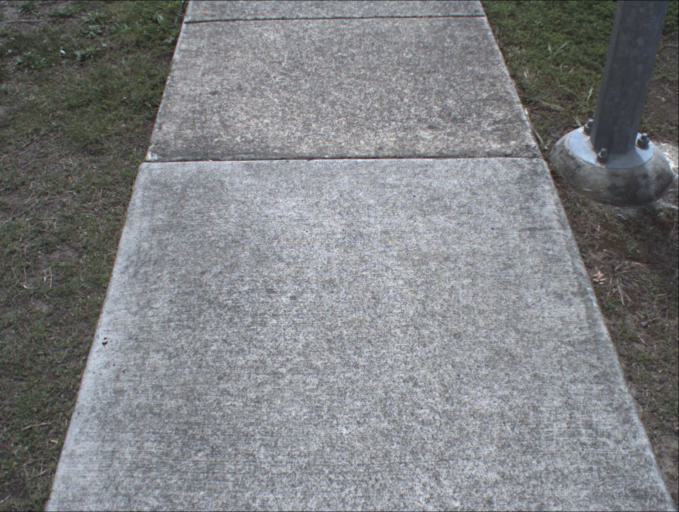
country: AU
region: Queensland
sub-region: Brisbane
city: Sunnybank Hills
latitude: -27.6655
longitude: 153.0499
